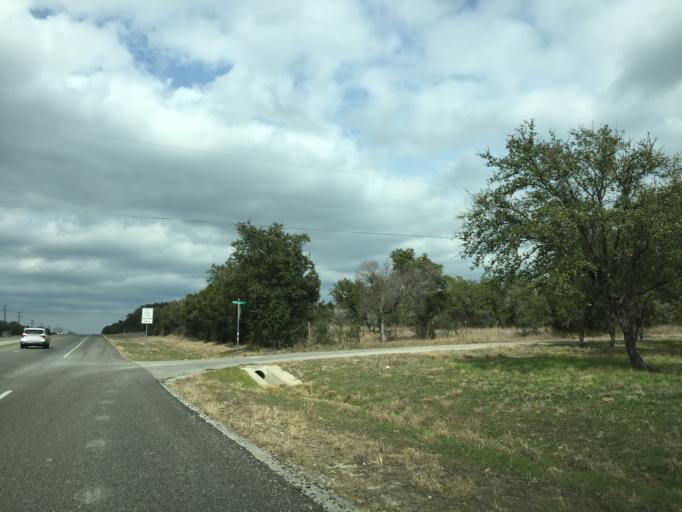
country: US
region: Texas
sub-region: Travis County
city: Briarcliff
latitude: 30.3785
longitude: -98.0816
